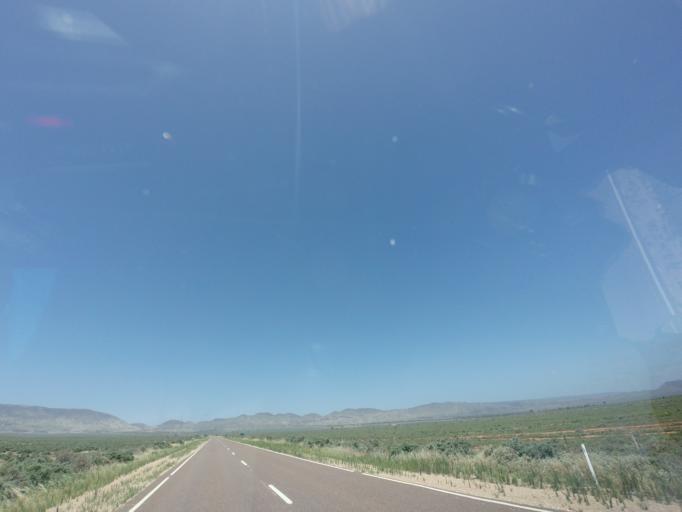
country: AU
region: South Australia
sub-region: Port Augusta
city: Port Augusta
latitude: -32.6261
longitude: 137.9355
